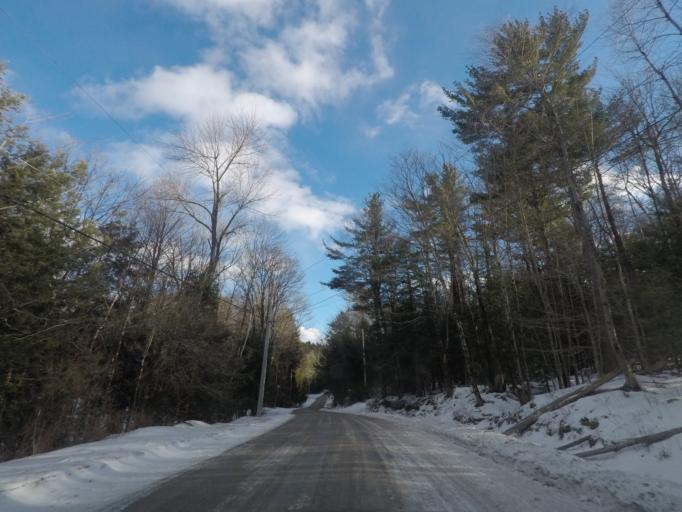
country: US
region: New York
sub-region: Rensselaer County
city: Poestenkill
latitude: 42.7510
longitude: -73.4849
